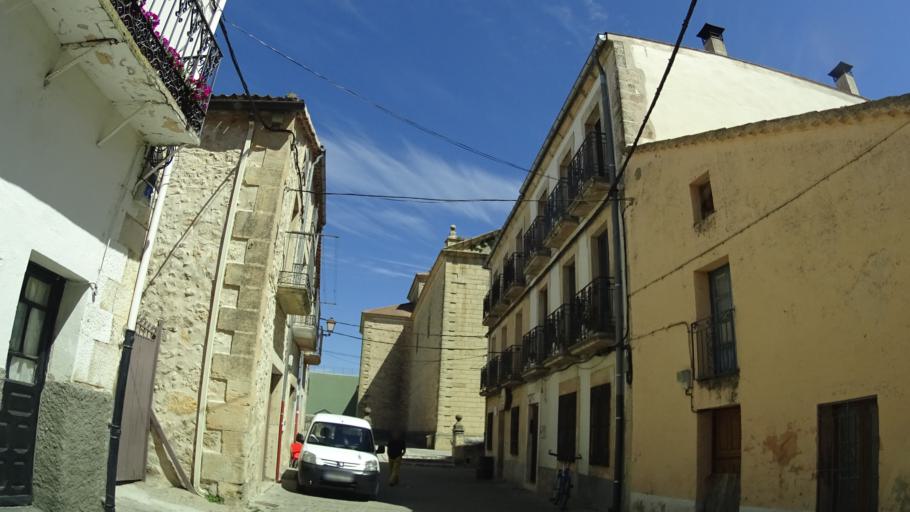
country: ES
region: Castille and Leon
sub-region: Provincia de Segovia
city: Pradena
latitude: 41.1397
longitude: -3.6888
